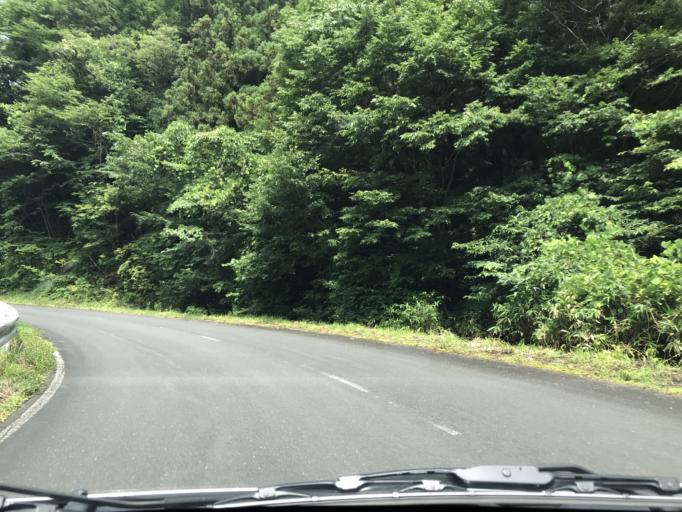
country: JP
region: Iwate
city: Mizusawa
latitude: 39.0619
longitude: 141.4030
